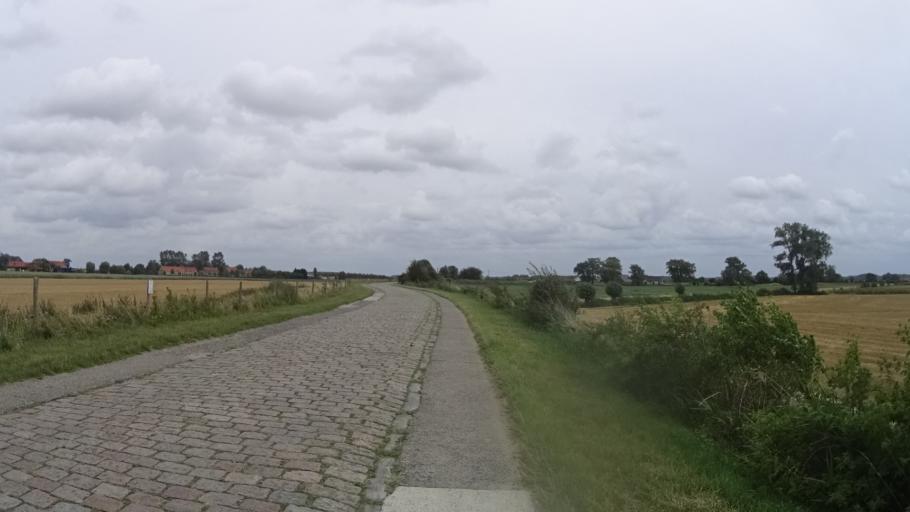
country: NL
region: Zeeland
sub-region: Gemeente Sluis
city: Sluis
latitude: 51.3378
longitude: 3.3437
